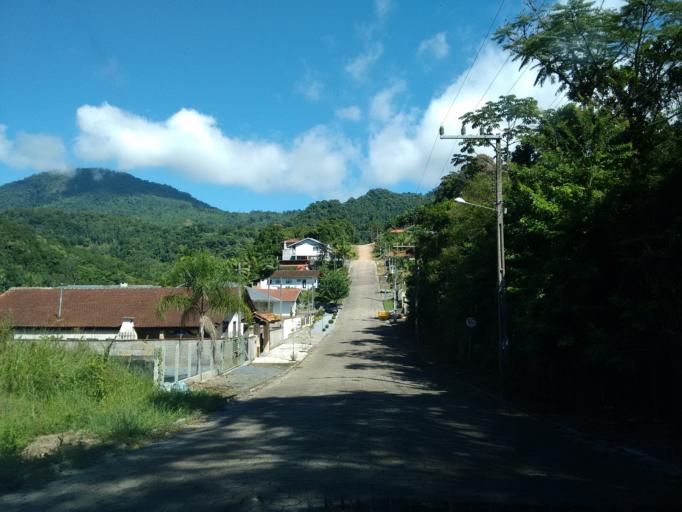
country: BR
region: Santa Catarina
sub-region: Pomerode
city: Pomerode
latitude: -26.7494
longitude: -49.1788
